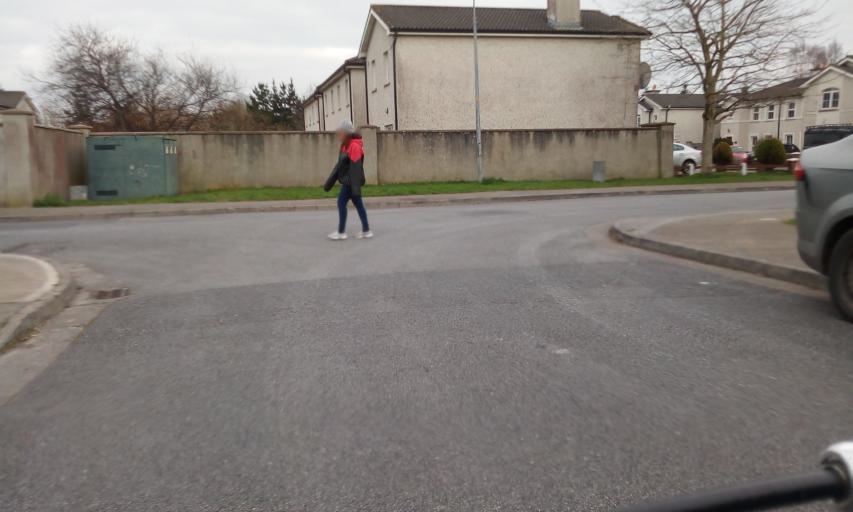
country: IE
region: Leinster
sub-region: Kilkenny
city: Kilkenny
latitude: 52.6651
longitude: -7.2300
